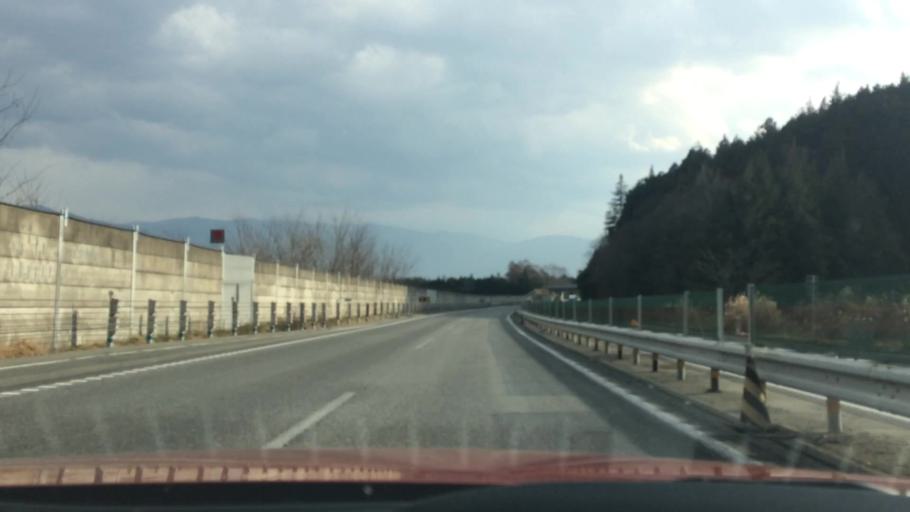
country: JP
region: Nagano
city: Ina
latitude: 35.7929
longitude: 137.9326
